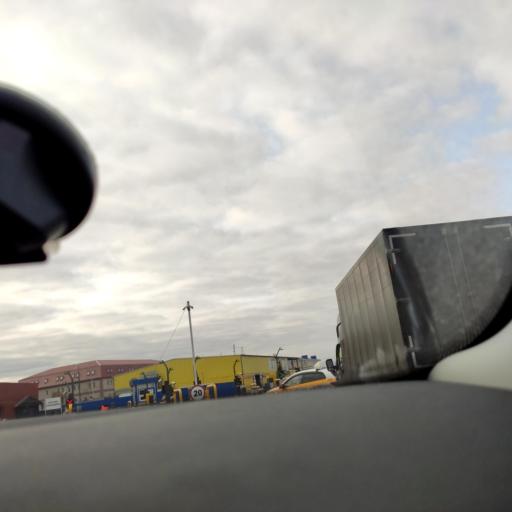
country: RU
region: Moskovskaya
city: Mosrentgen
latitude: 55.6252
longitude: 37.4666
